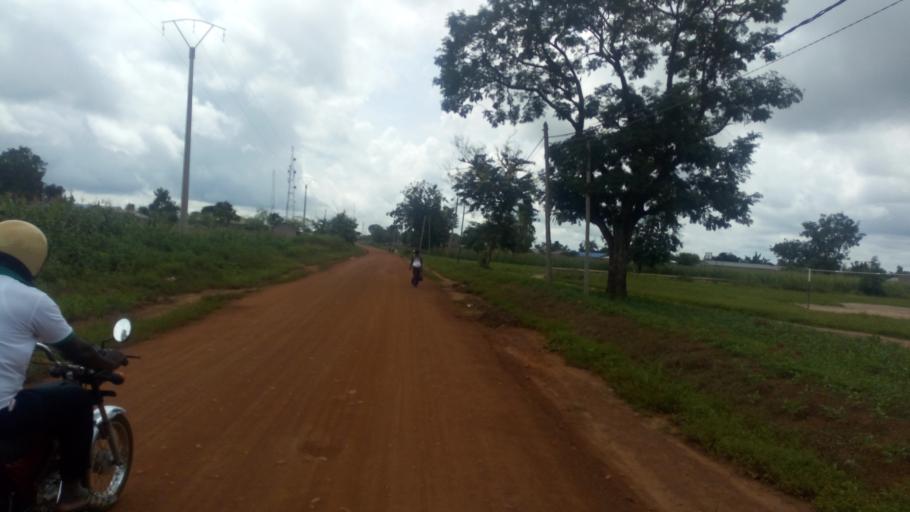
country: TG
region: Centrale
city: Sotouboua
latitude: 8.5567
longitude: 0.9983
